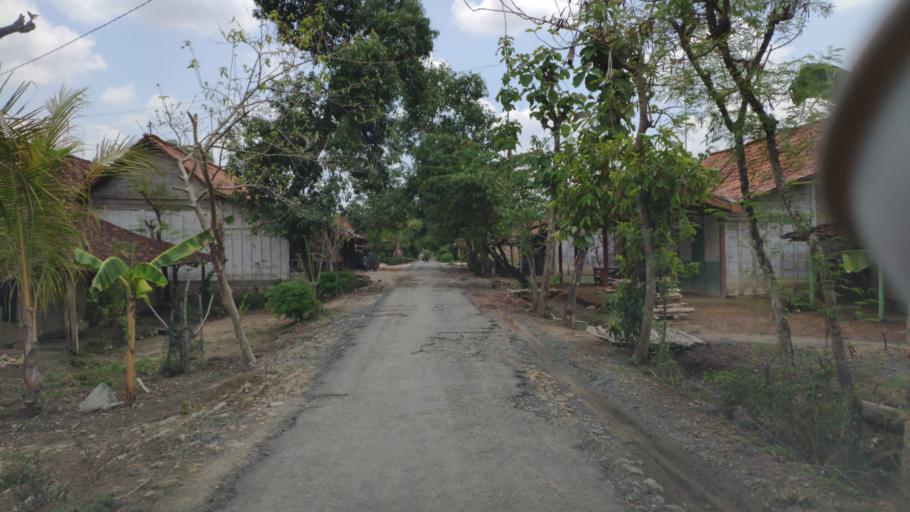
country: ID
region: Central Java
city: Gumiring
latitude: -7.0387
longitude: 111.3875
